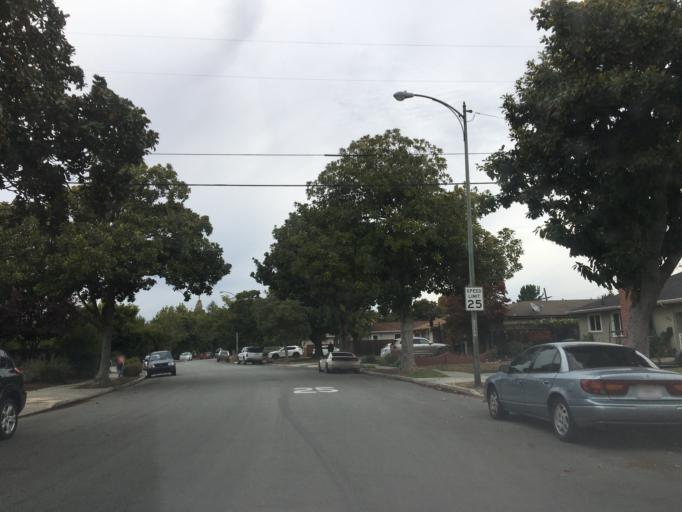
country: US
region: California
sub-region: Santa Clara County
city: Sunnyvale
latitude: 37.3914
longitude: -122.0226
